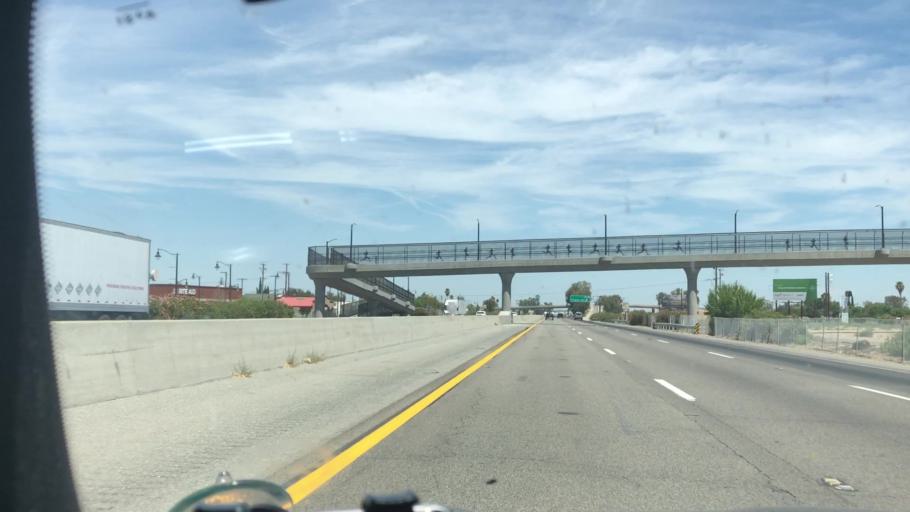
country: US
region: California
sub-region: Kern County
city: McFarland
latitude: 35.6770
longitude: -119.2272
